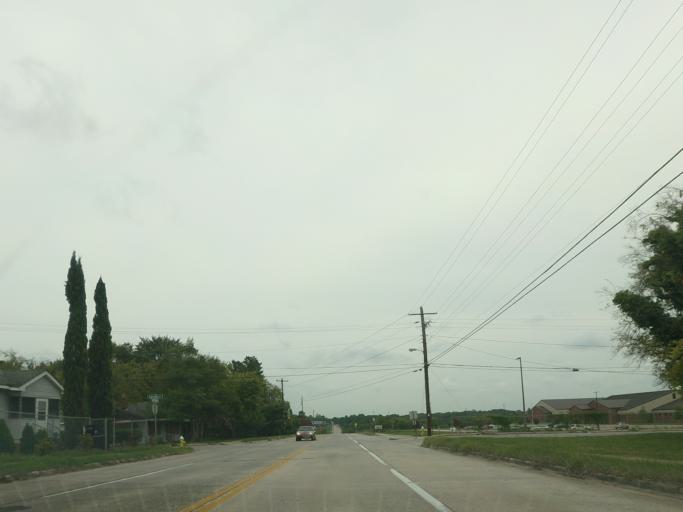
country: US
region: Georgia
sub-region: Bibb County
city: Macon
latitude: 32.8202
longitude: -83.6596
